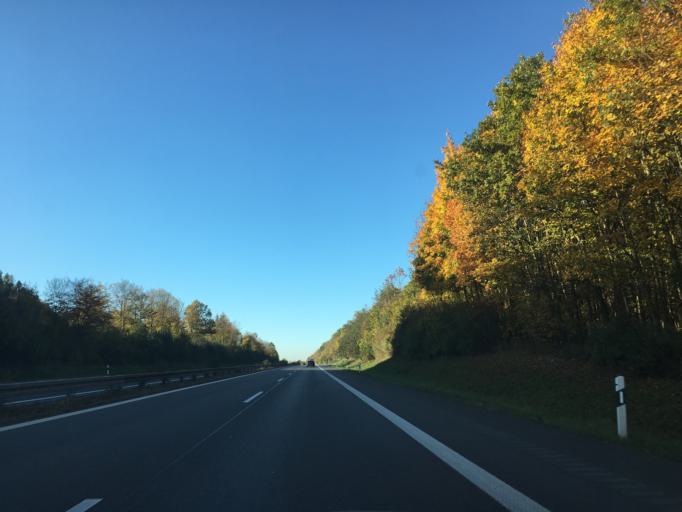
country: DE
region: Baden-Wuerttemberg
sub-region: Freiburg Region
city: Steisslingen
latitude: 47.7795
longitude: 8.8993
